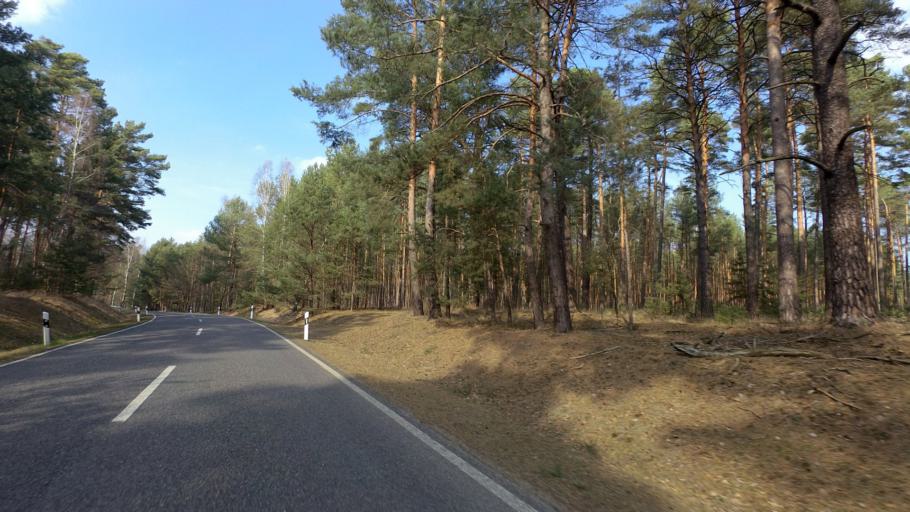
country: DE
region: Brandenburg
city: Dahme
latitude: 51.9474
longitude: 13.4404
